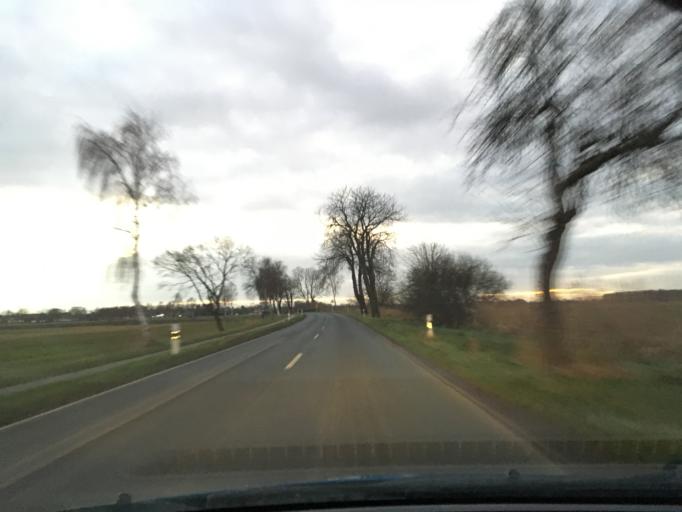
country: DE
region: Lower Saxony
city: Tespe
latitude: 53.3806
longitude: 10.4176
